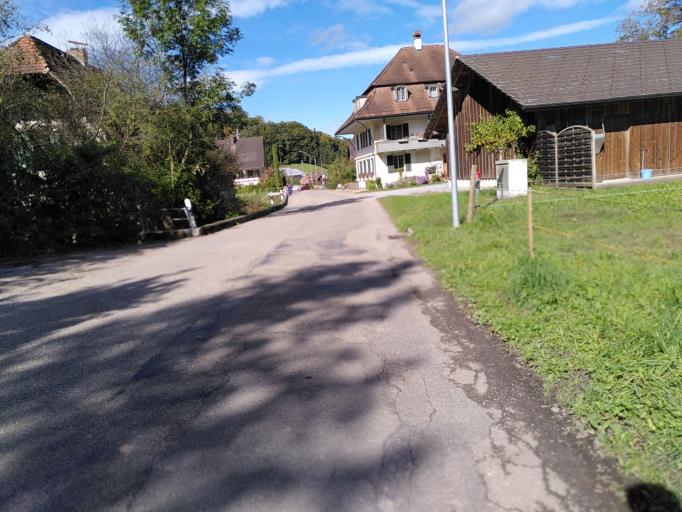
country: CH
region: Bern
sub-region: Oberaargau
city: Seeberg
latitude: 47.1409
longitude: 7.6986
